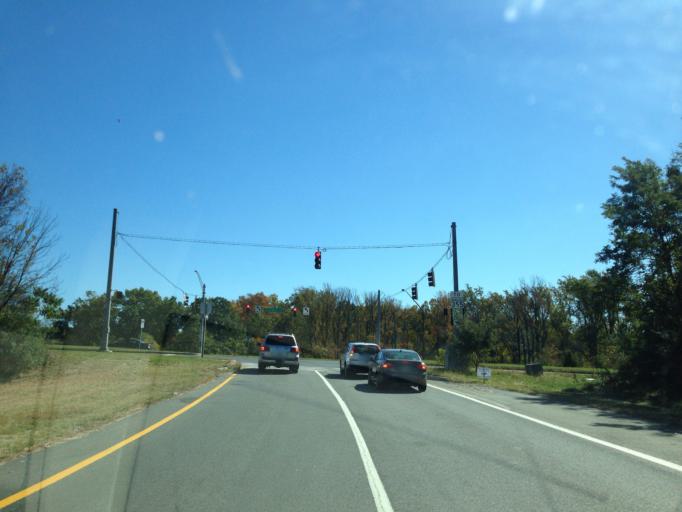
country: US
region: Maryland
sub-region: Montgomery County
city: Germantown
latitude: 39.1970
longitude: -77.2660
